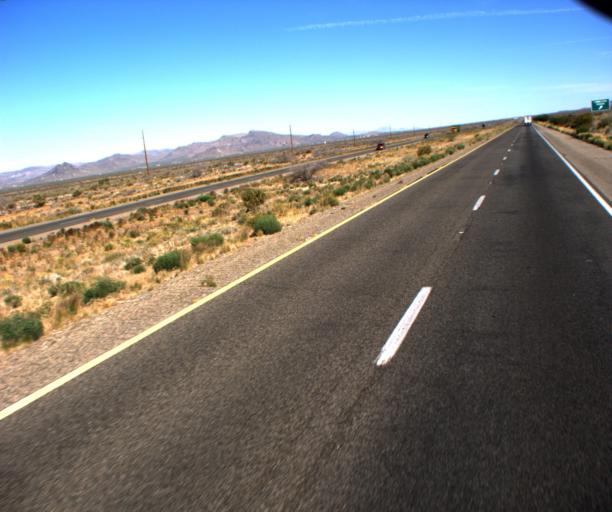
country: US
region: Arizona
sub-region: Mohave County
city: Golden Valley
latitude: 35.2921
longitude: -114.1832
